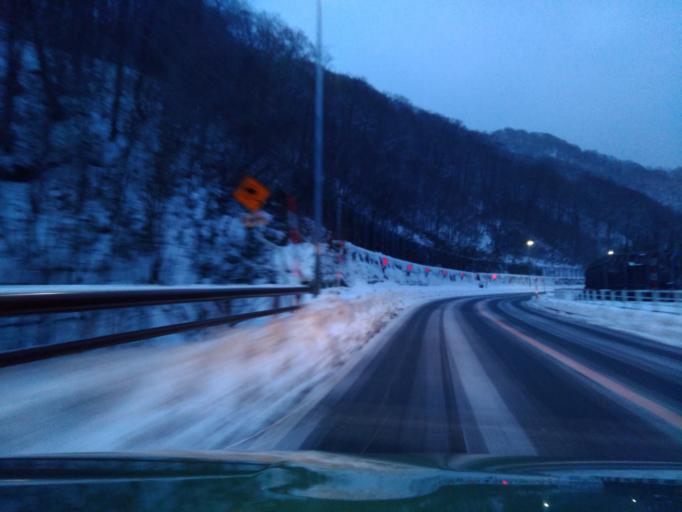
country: JP
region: Iwate
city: Shizukuishi
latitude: 39.7190
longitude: 140.8213
